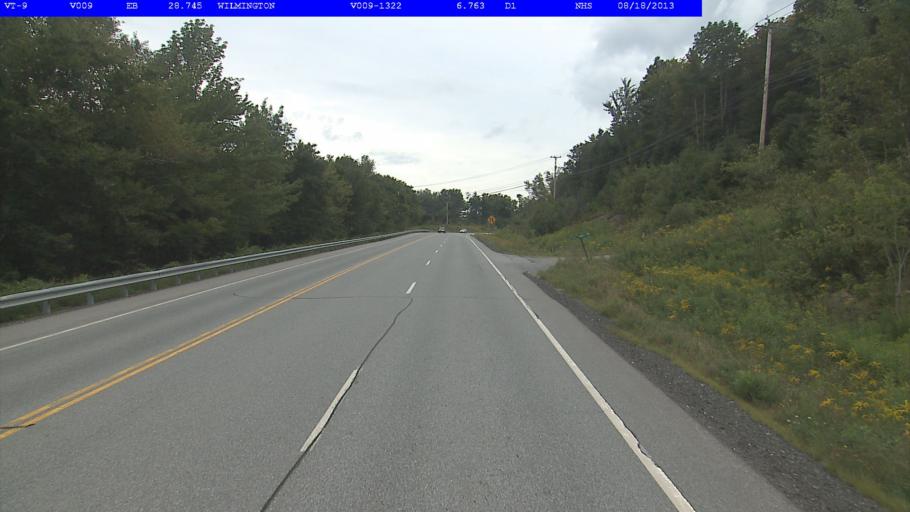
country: US
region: Vermont
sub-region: Windham County
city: Dover
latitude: 42.8575
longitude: -72.8085
